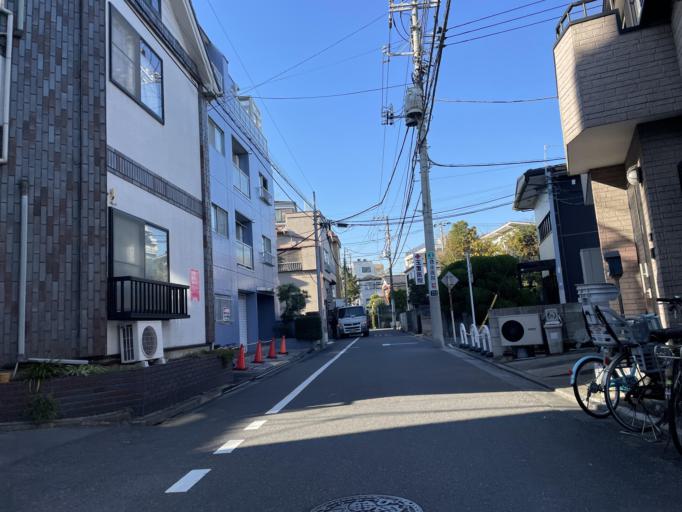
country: JP
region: Tokyo
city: Urayasu
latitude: 35.7249
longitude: 139.8853
